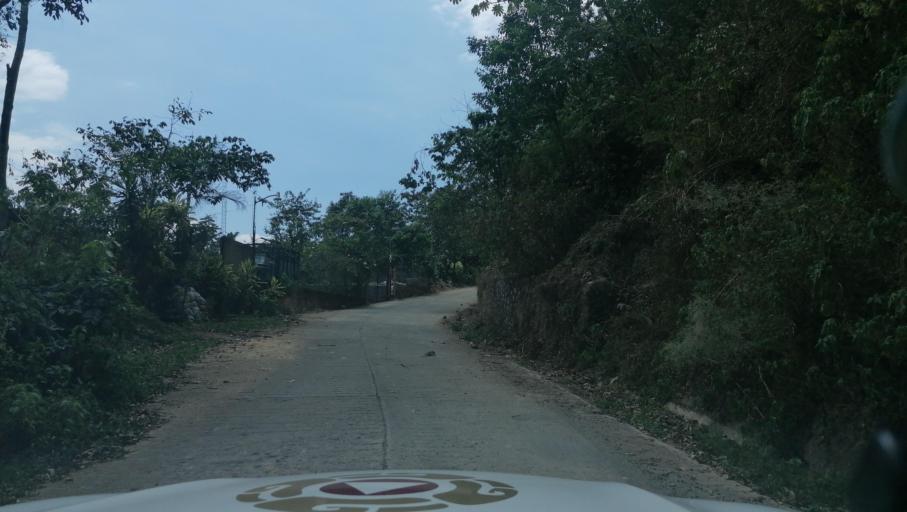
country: MX
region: Chiapas
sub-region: Cacahoatan
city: Benito Juarez
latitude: 15.1098
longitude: -92.2079
